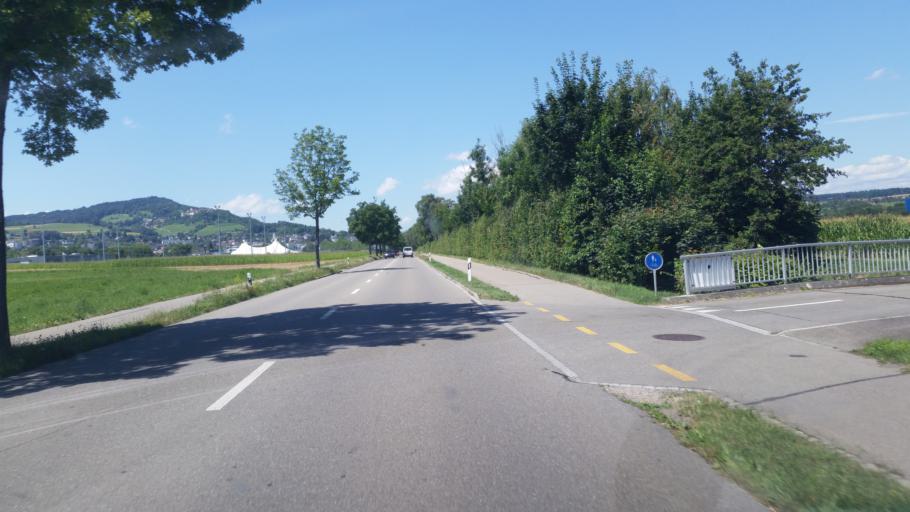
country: CH
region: Zurich
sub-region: Bezirk Dielsdorf
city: Niederhasli
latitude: 47.4817
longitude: 8.4804
